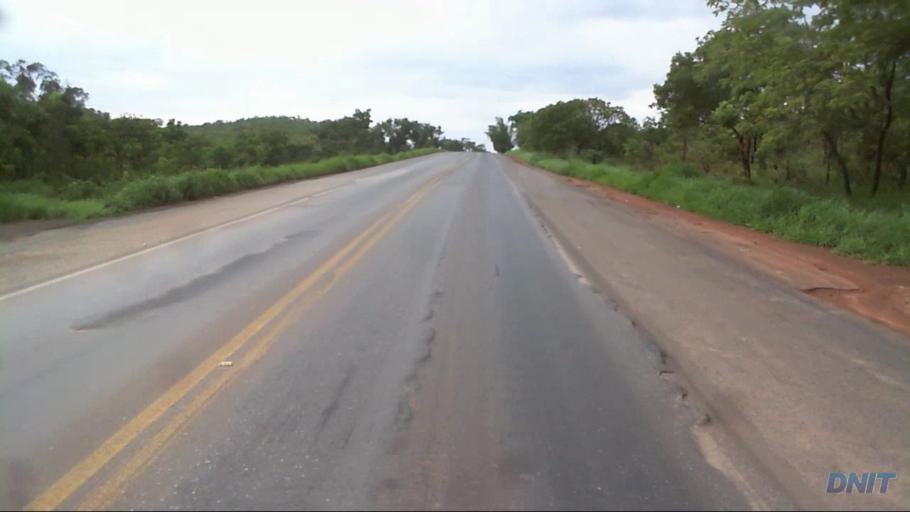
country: BR
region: Goias
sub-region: Uruacu
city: Uruacu
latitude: -14.5617
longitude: -49.1569
